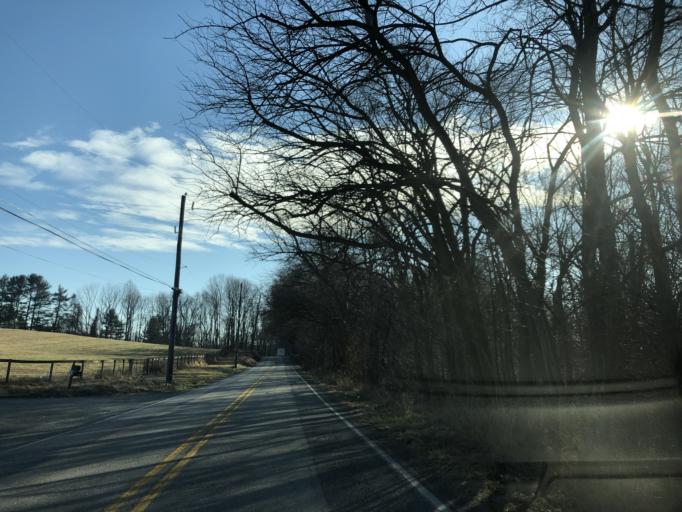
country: US
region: Pennsylvania
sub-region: Chester County
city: Upland
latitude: 39.8800
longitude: -75.7743
